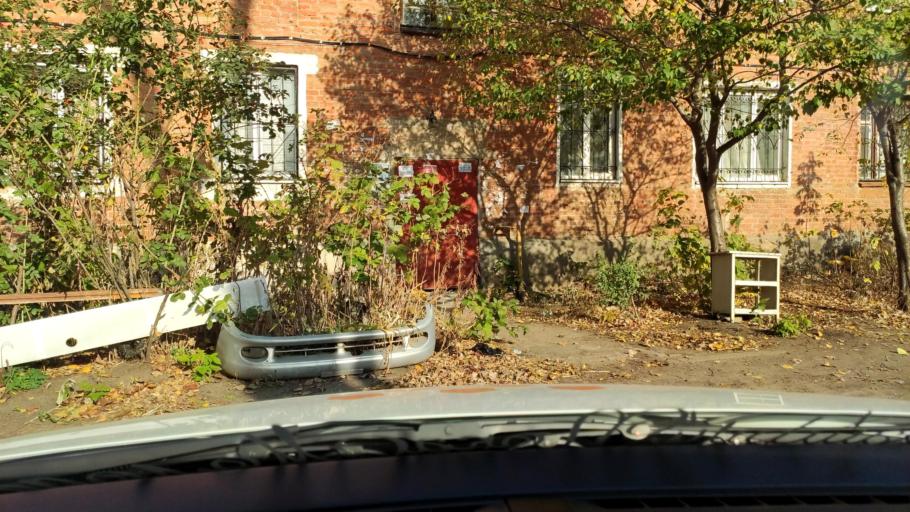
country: RU
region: Voronezj
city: Voronezh
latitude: 51.6773
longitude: 39.1409
